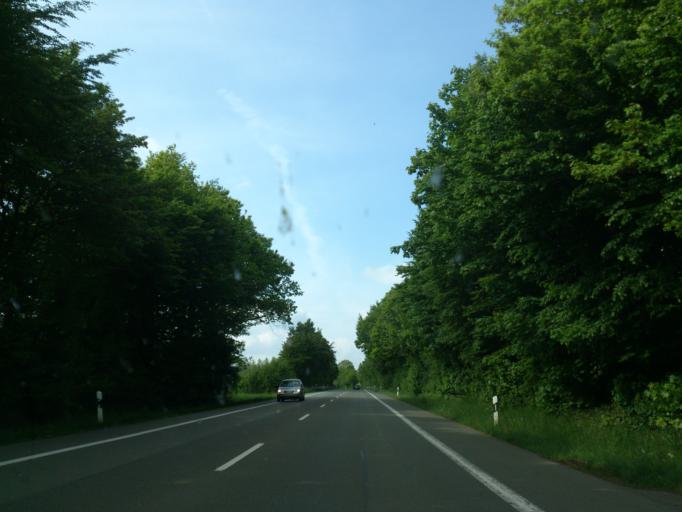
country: DE
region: North Rhine-Westphalia
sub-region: Regierungsbezirk Detmold
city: Willebadessen
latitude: 51.6603
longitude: 9.0077
